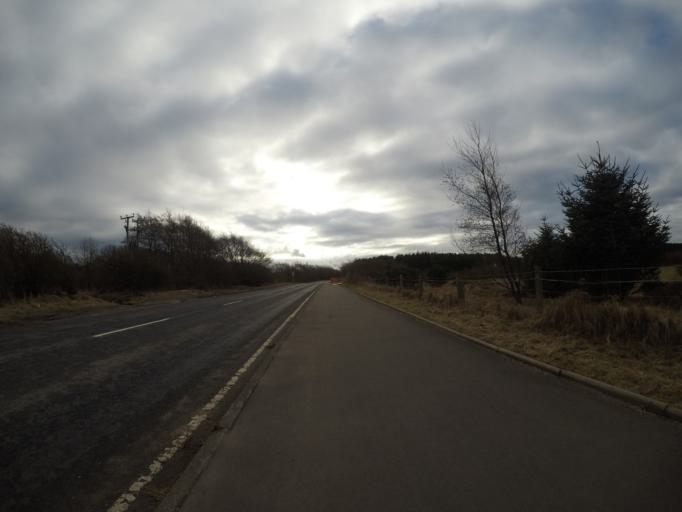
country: GB
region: Scotland
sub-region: North Ayrshire
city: Irvine
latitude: 55.5928
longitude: -4.6533
